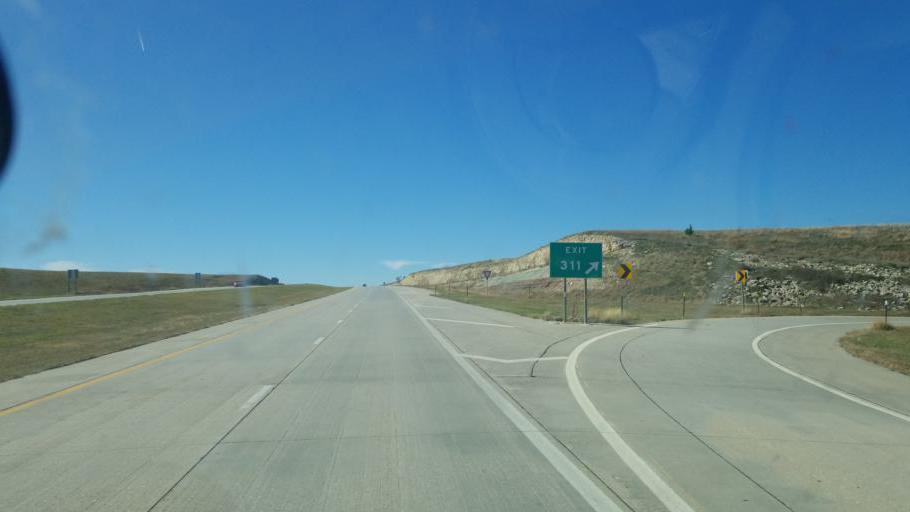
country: US
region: Kansas
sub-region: Riley County
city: Manhattan
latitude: 39.0659
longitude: -96.5777
